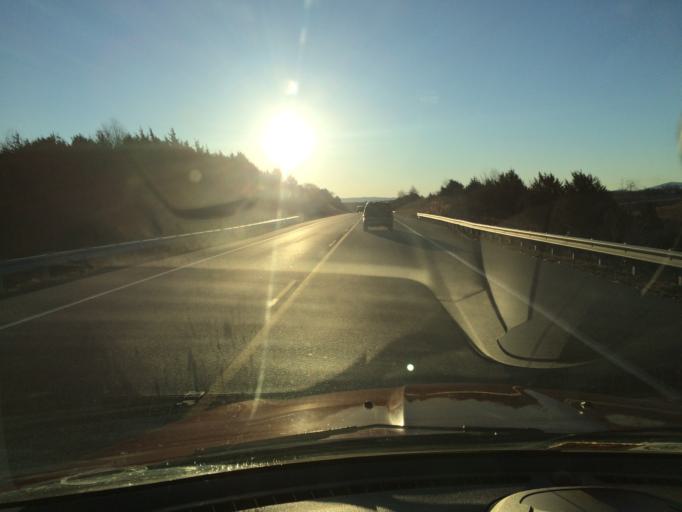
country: US
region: Virginia
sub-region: Augusta County
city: Verona
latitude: 38.1760
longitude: -79.0246
